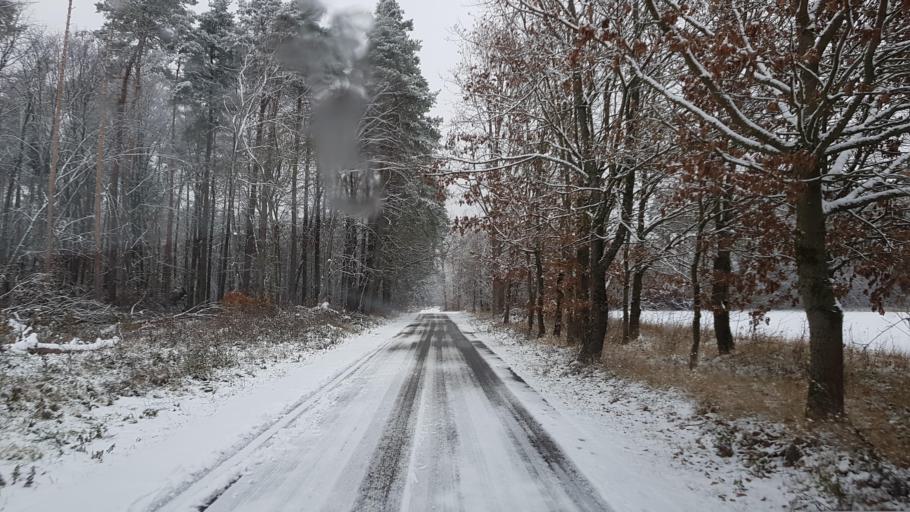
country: PL
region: West Pomeranian Voivodeship
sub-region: Powiat lobeski
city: Resko
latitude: 53.7781
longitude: 15.5318
